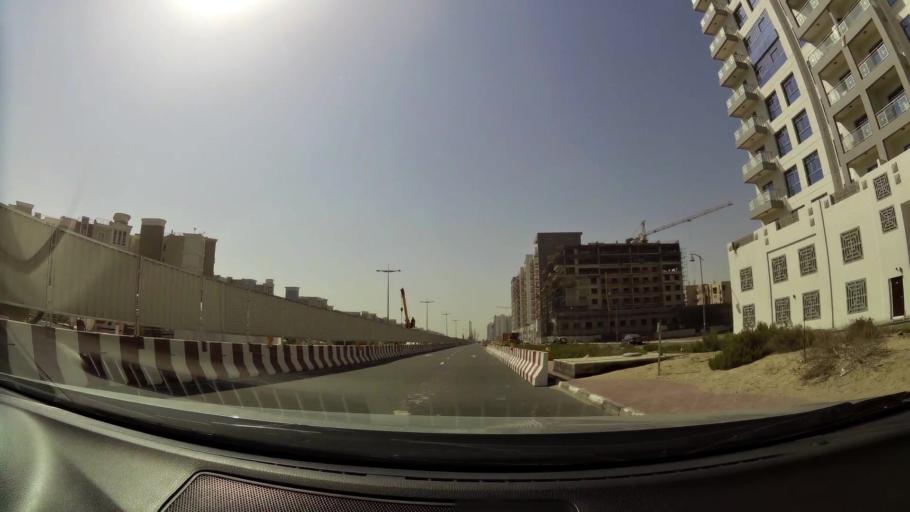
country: AE
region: Dubai
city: Dubai
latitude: 25.0336
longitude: 55.1477
